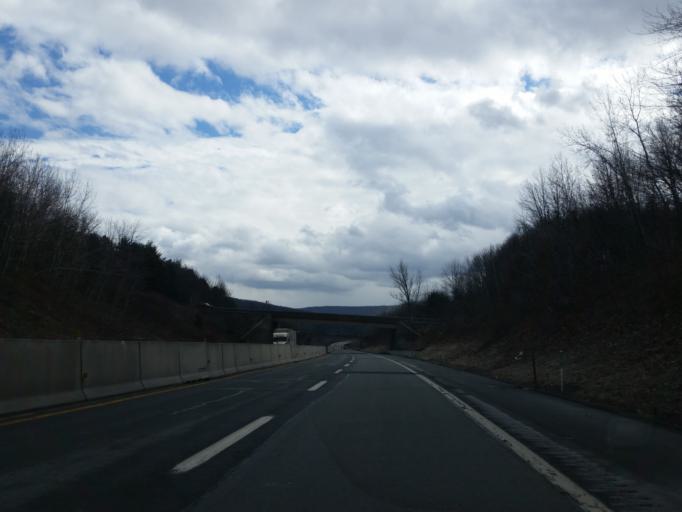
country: US
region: Pennsylvania
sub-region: Lackawanna County
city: Moosic
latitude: 41.3585
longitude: -75.7172
